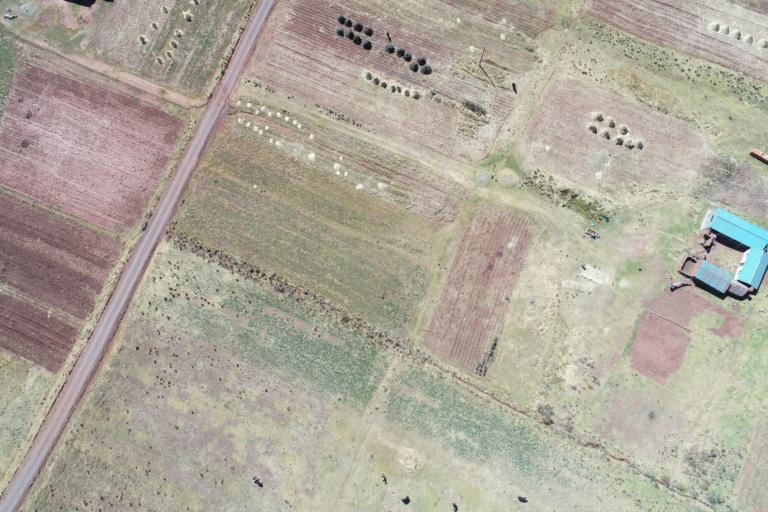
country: BO
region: La Paz
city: Tiahuanaco
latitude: -16.5943
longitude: -68.7584
